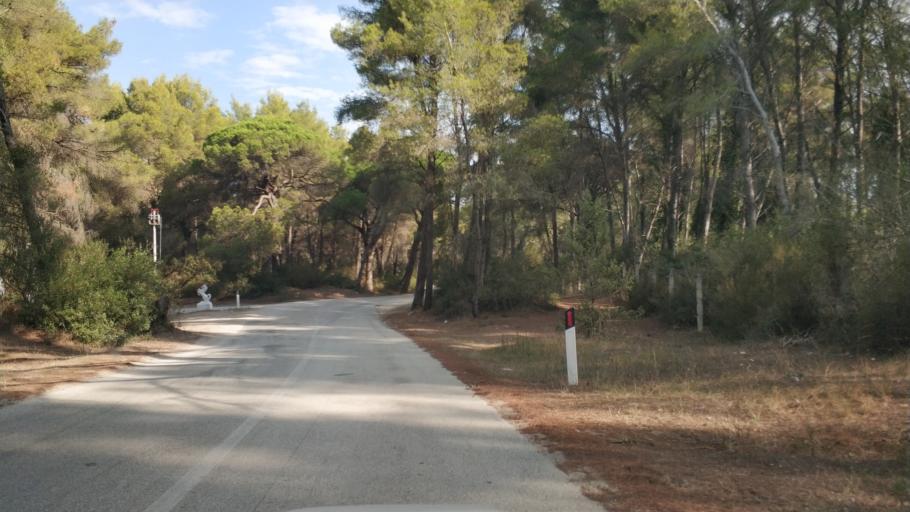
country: AL
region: Fier
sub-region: Rrethi i Lushnjes
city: Divjake
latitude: 40.9798
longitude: 19.4820
